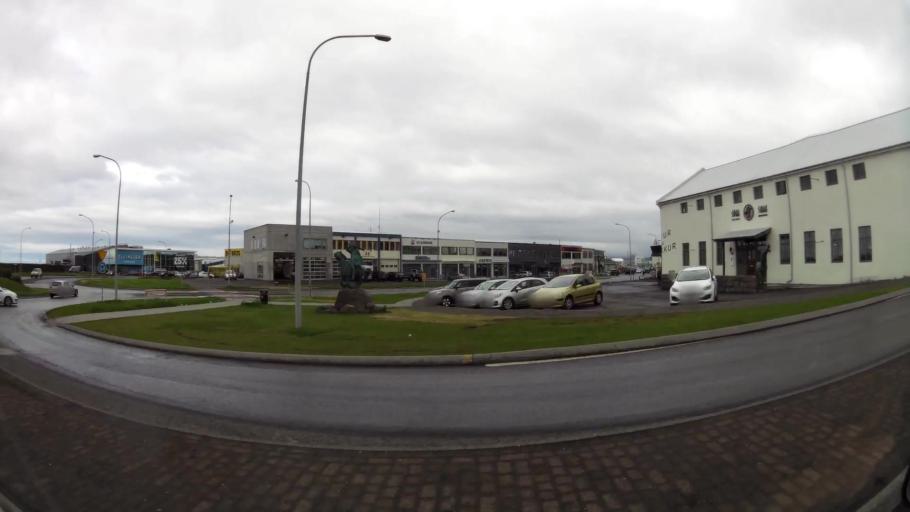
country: IS
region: Capital Region
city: Seltjarnarnes
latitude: 64.1524
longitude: -21.9521
